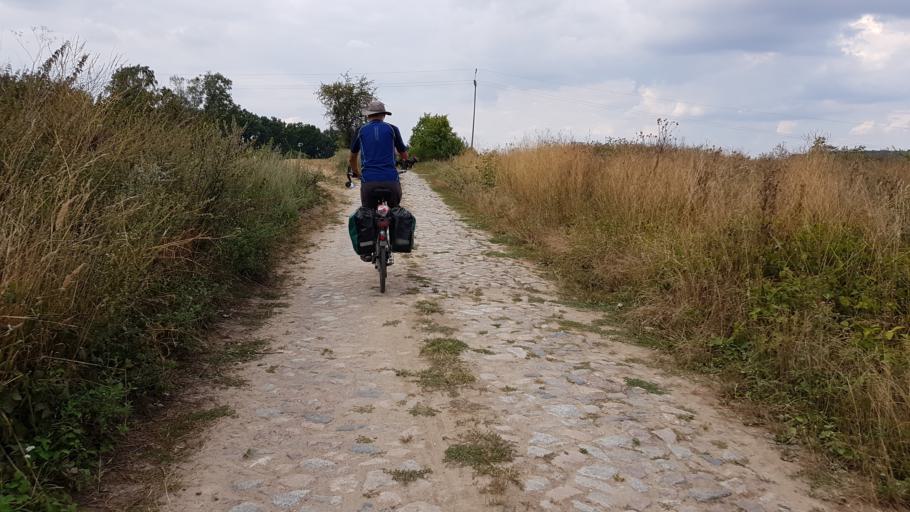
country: PL
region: West Pomeranian Voivodeship
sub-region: Powiat mysliborski
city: Barlinek
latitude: 53.0758
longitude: 15.2037
